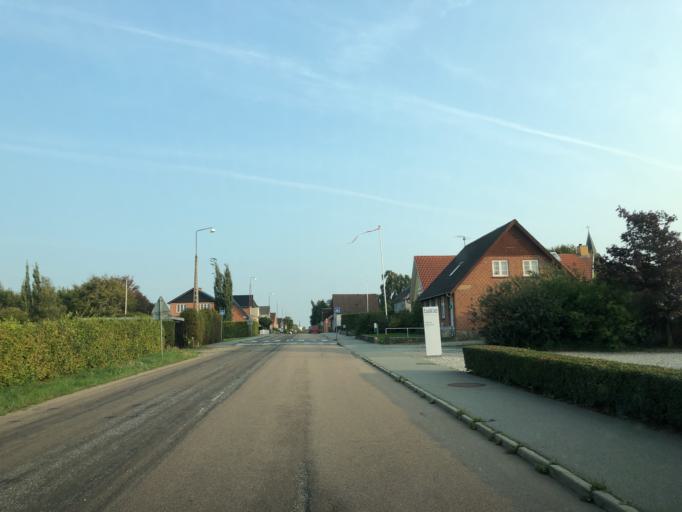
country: DK
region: South Denmark
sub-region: Vejle Kommune
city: Jelling
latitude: 55.7109
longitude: 9.3741
